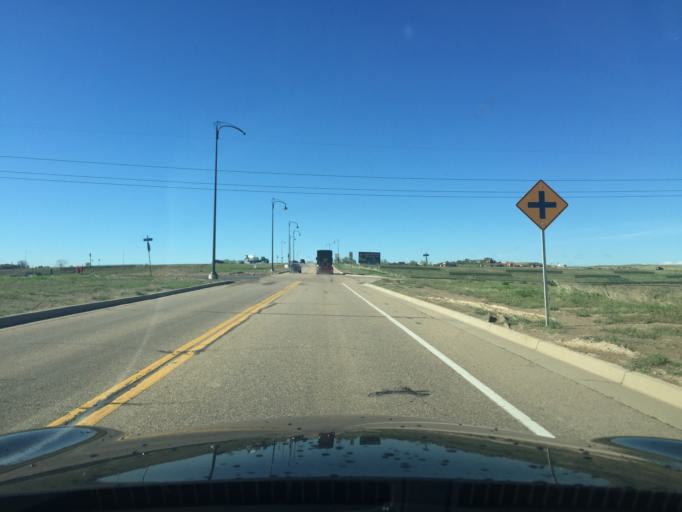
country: US
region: Colorado
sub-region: Boulder County
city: Erie
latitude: 39.9875
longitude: -105.0178
